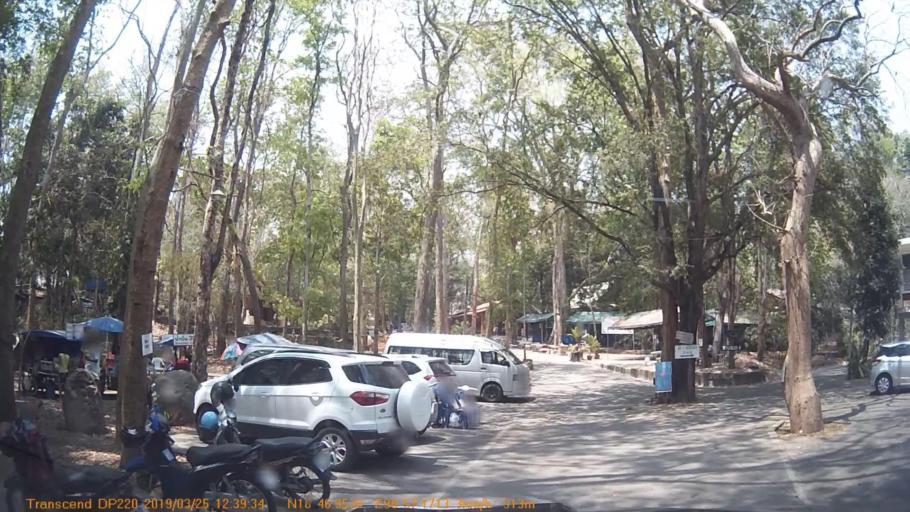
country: TH
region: Chiang Mai
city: Chiang Mai
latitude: 18.7826
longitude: 98.9528
